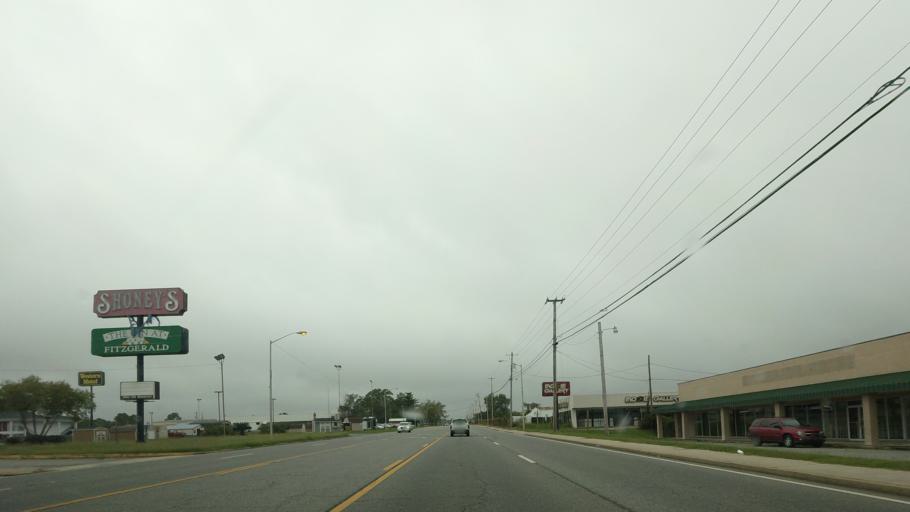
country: US
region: Georgia
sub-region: Ben Hill County
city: Fitzgerald
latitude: 31.6960
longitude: -83.2475
